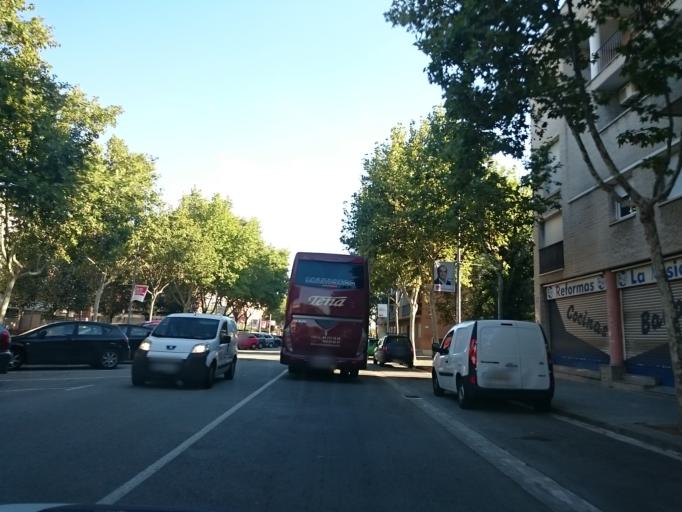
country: ES
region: Catalonia
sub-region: Provincia de Barcelona
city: Palleja
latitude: 41.4223
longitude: 2.0002
